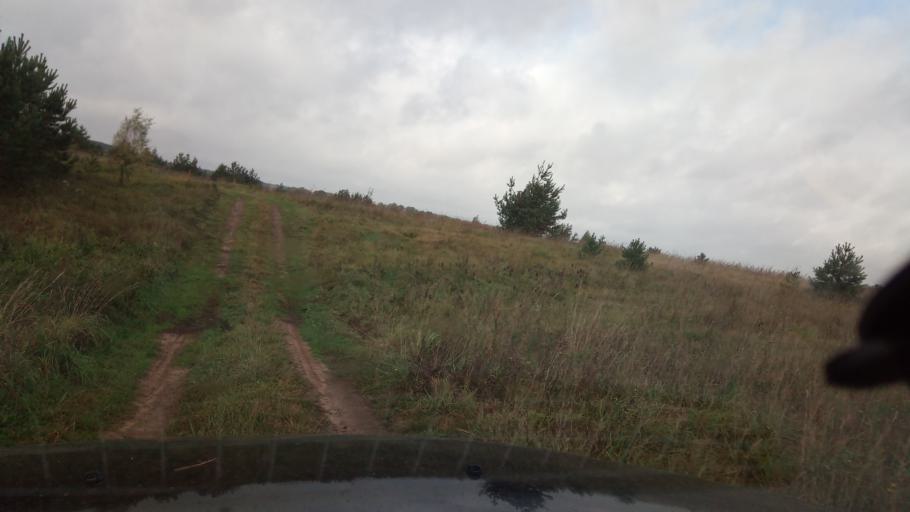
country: LT
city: Skaidiskes
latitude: 54.6188
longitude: 25.5170
